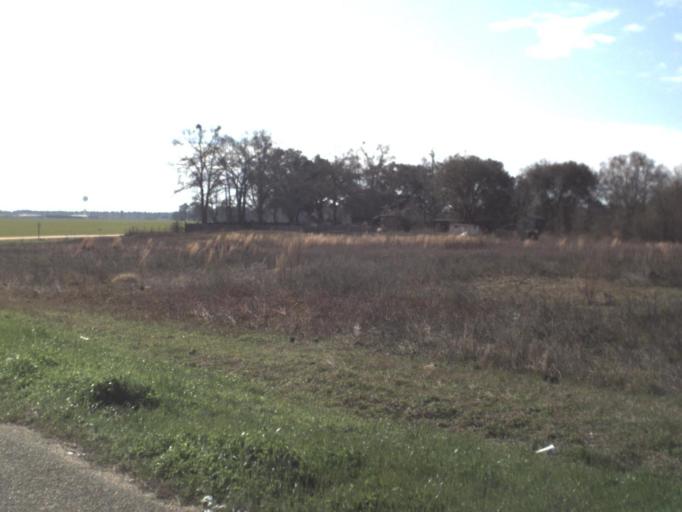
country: US
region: Florida
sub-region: Jackson County
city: Malone
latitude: 30.9804
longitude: -85.1773
